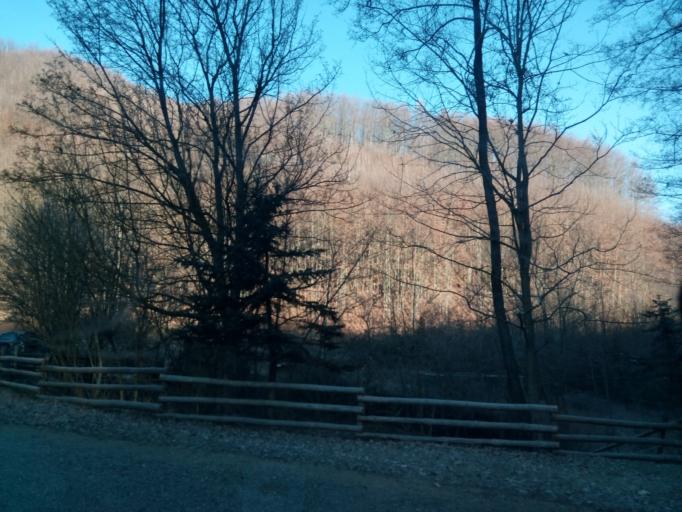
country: SK
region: Kosicky
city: Medzev
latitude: 48.6754
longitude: 20.8769
